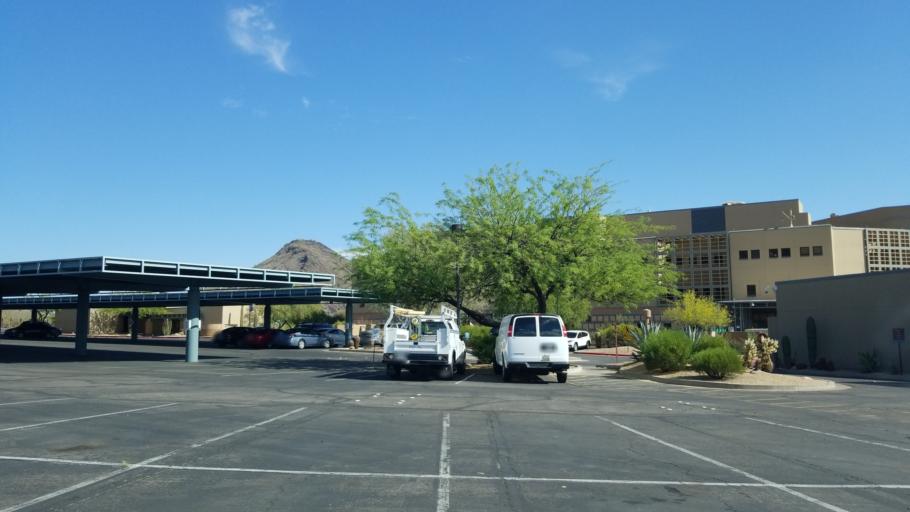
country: US
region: Arizona
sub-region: Maricopa County
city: Fountain Hills
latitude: 33.5871
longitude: -111.7945
